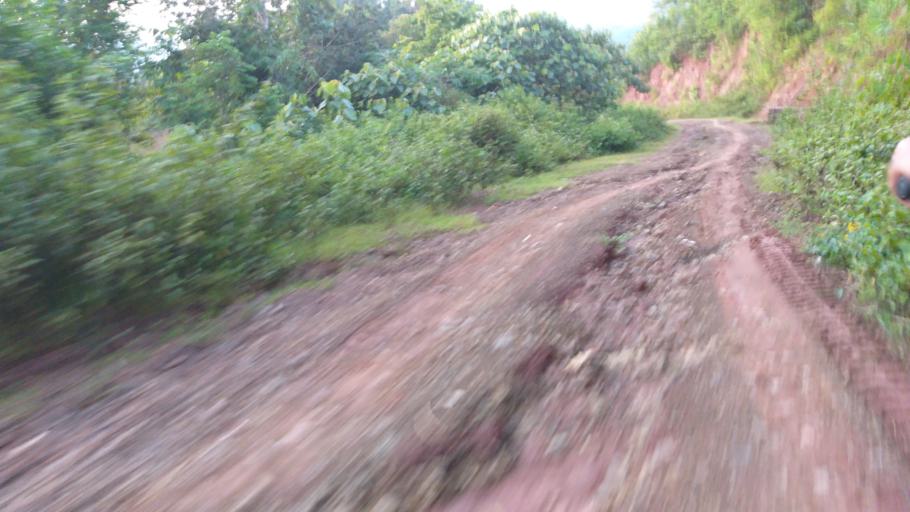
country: LA
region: Phongsali
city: Khoa
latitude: 21.4011
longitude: 102.6369
